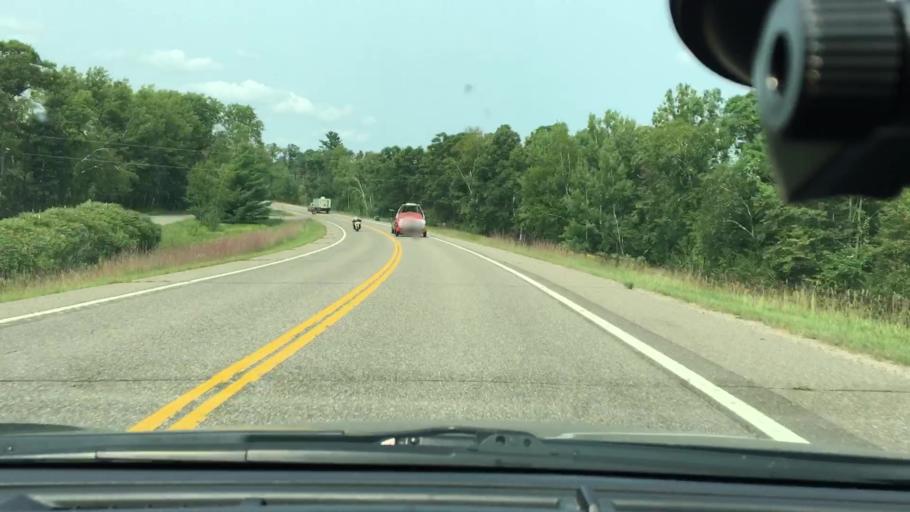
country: US
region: Minnesota
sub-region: Cass County
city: East Gull Lake
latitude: 46.4006
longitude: -94.3505
